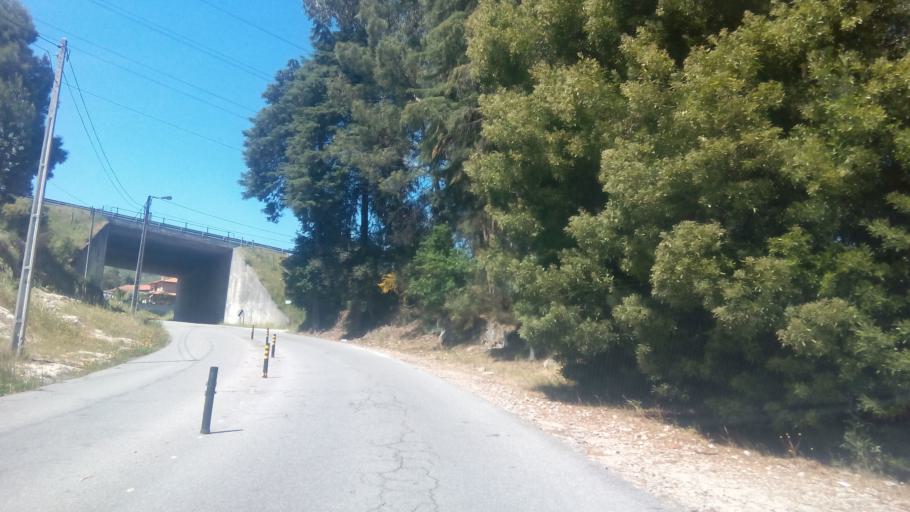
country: PT
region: Porto
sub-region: Paredes
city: Baltar
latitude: 41.1892
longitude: -8.3606
